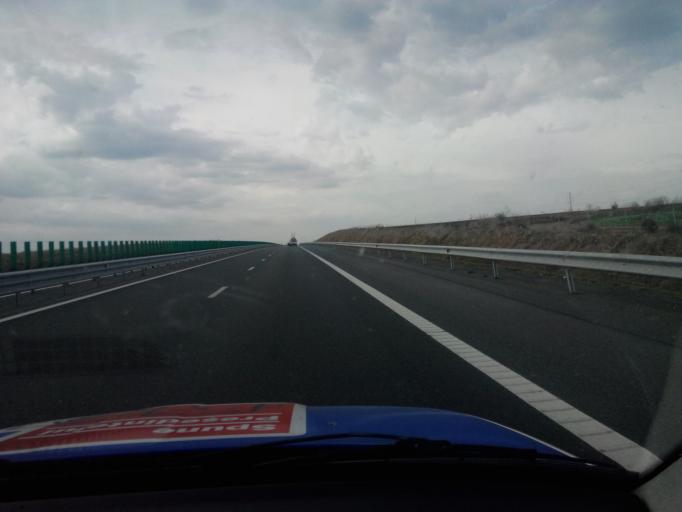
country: RO
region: Constanta
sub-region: Comuna Valu lui Traian
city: Valu lui Traian
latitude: 44.1419
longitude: 28.4945
